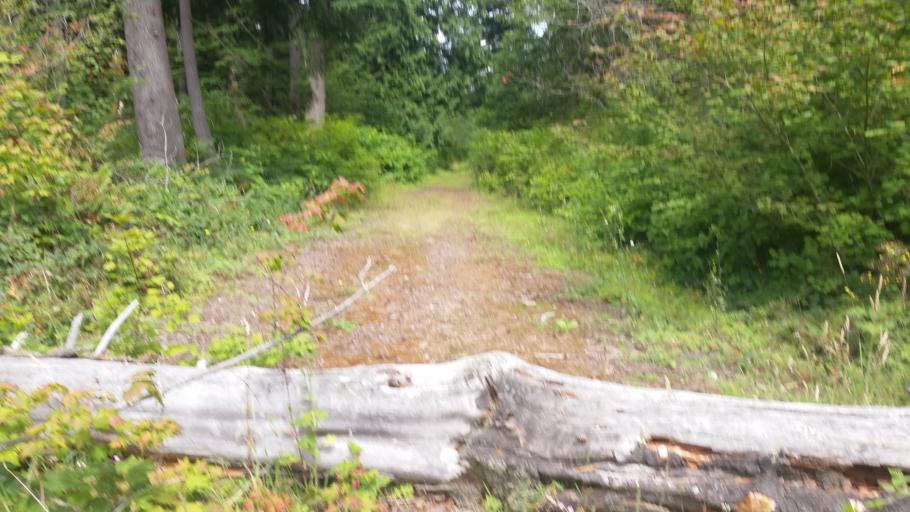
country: US
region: Washington
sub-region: King County
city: Union Hill-Novelty Hill
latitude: 47.6939
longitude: -122.0352
